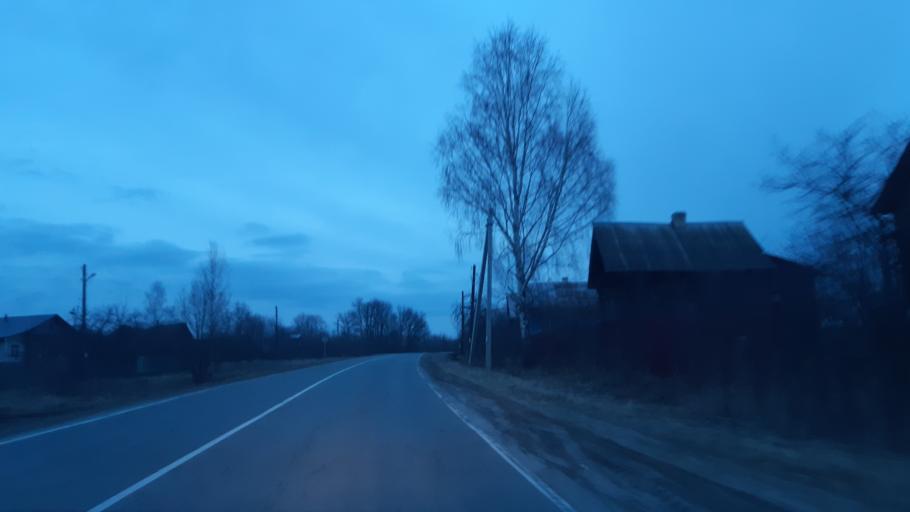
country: RU
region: Vladimir
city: Luknovo
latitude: 56.1860
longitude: 42.0176
